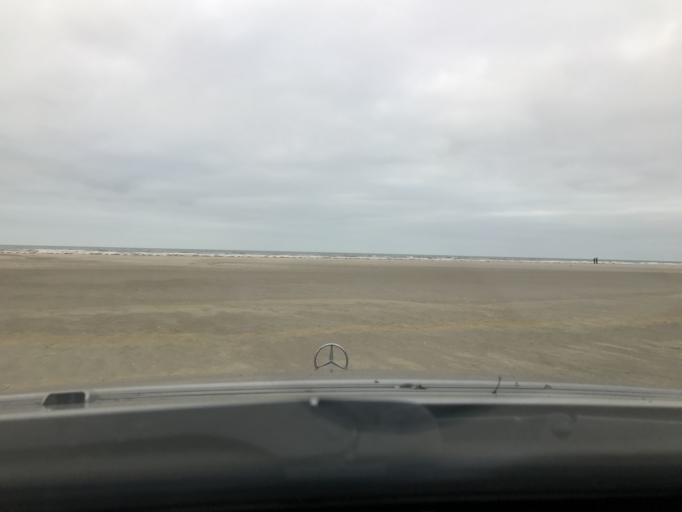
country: DE
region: Schleswig-Holstein
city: List
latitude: 55.1502
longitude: 8.4789
